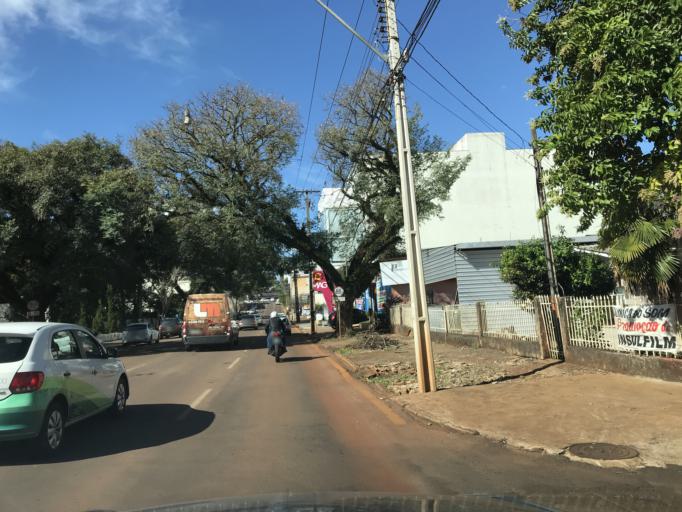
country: BR
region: Parana
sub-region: Cascavel
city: Cascavel
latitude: -24.9562
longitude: -53.4669
